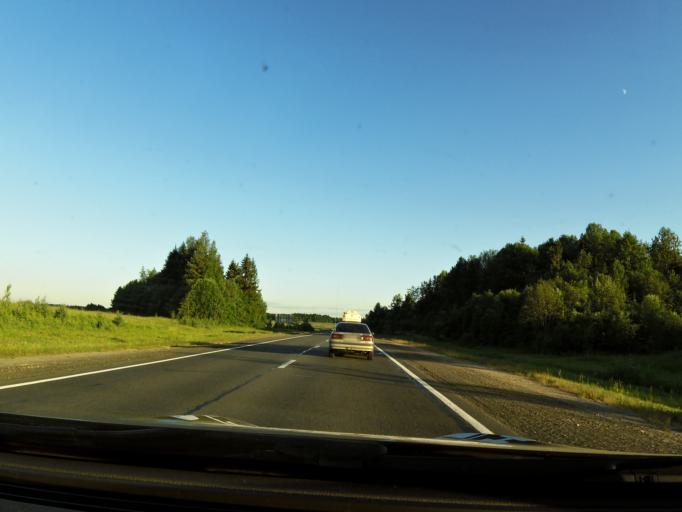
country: RU
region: Vologda
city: Gryazovets
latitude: 58.8452
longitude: 40.2041
